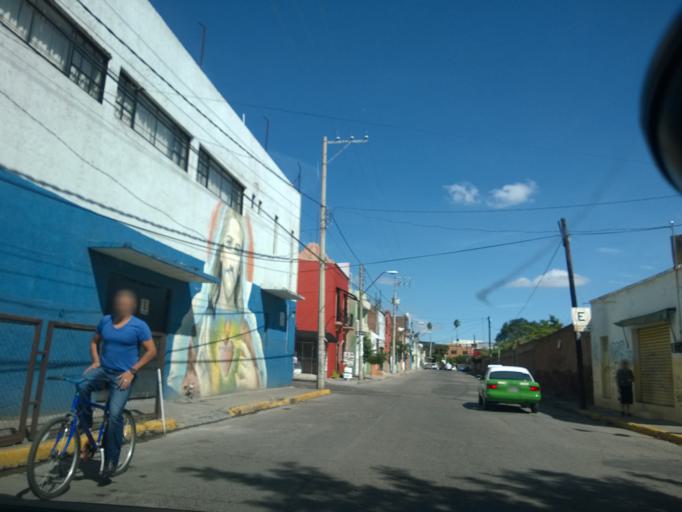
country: MX
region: Guanajuato
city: Leon
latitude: 21.1122
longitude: -101.6796
